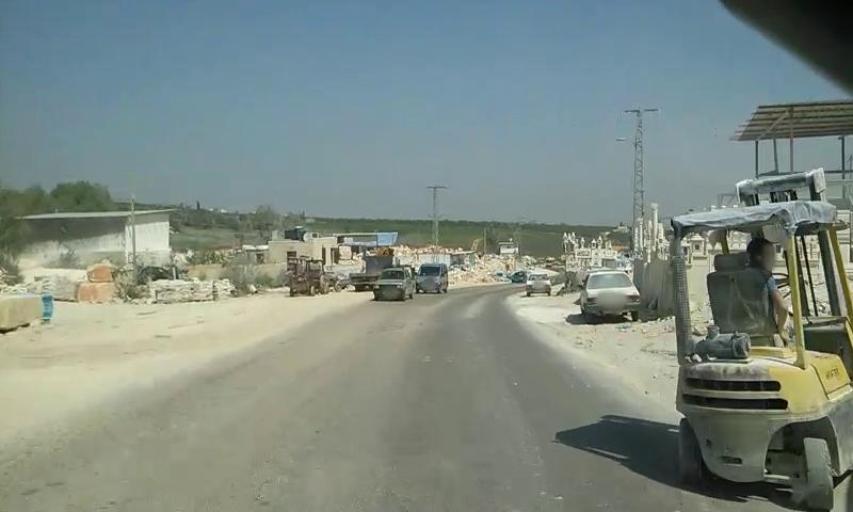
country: PS
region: West Bank
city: Ash Shuhada'
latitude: 32.4371
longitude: 35.2733
